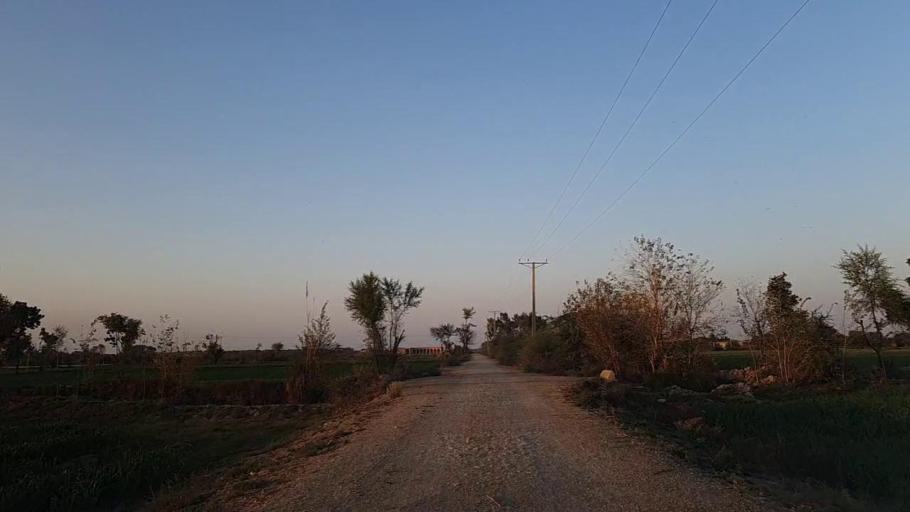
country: PK
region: Sindh
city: Jam Sahib
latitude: 26.3115
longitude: 68.6536
